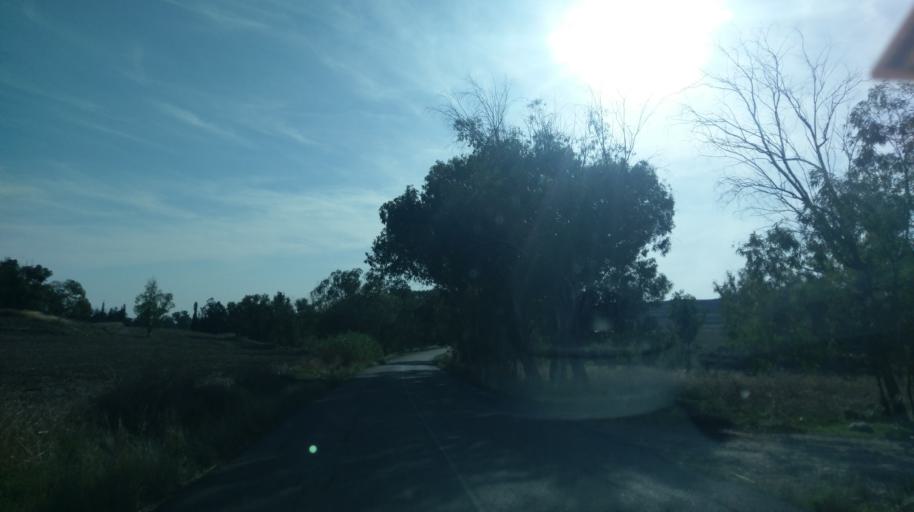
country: CY
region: Ammochostos
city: Lefkonoiko
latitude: 35.2946
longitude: 33.7384
